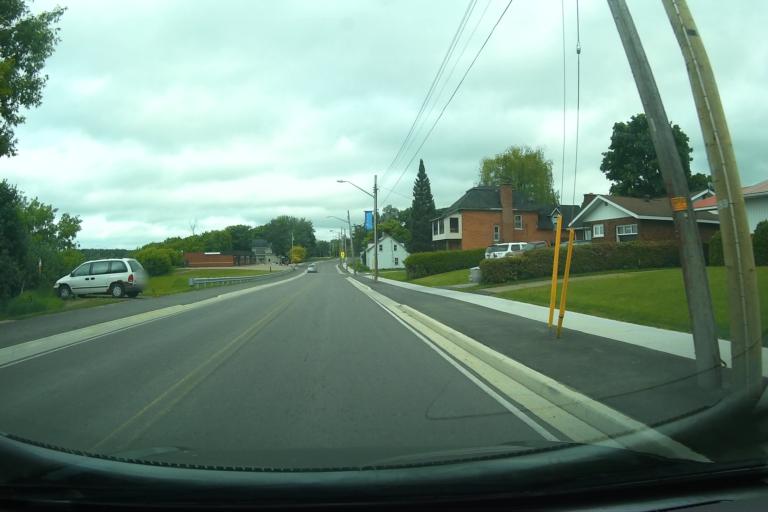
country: CA
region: Ontario
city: Pembroke
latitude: 45.5372
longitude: -77.0993
